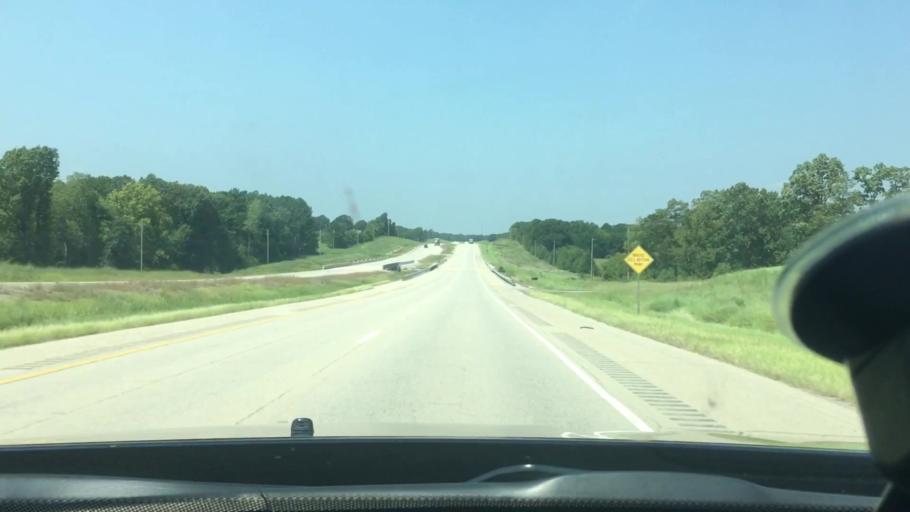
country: US
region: Oklahoma
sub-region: Atoka County
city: Atoka
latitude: 34.3090
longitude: -96.0122
